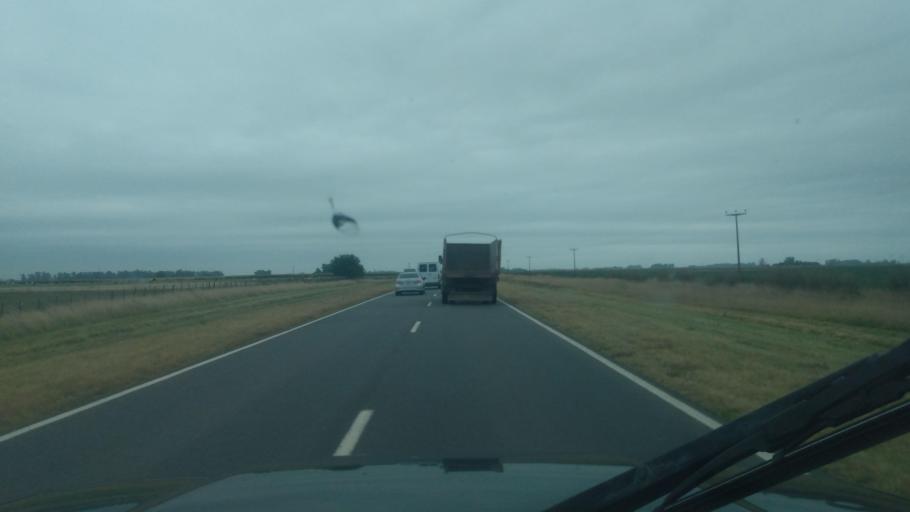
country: AR
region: Buenos Aires
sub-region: Partido de Nueve de Julio
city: Nueve de Julio
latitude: -35.3896
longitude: -60.7366
